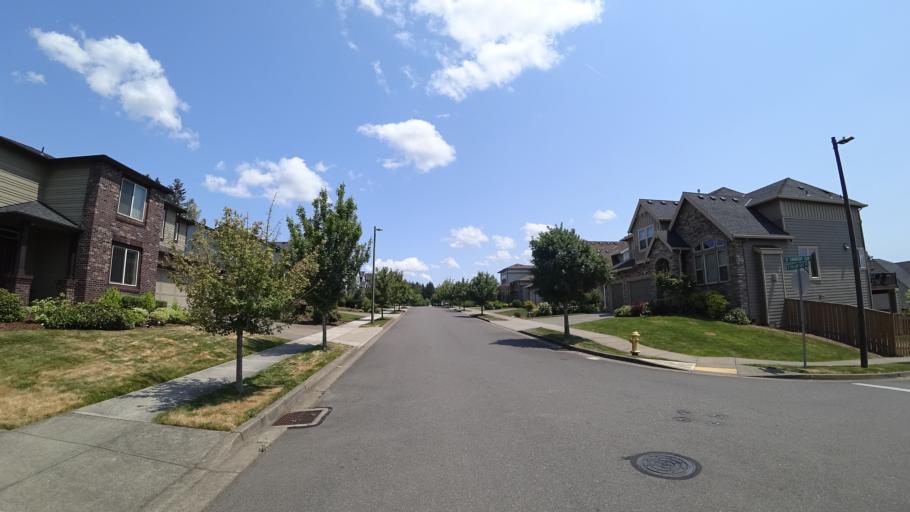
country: US
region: Oregon
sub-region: Clackamas County
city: Happy Valley
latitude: 45.4464
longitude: -122.5512
